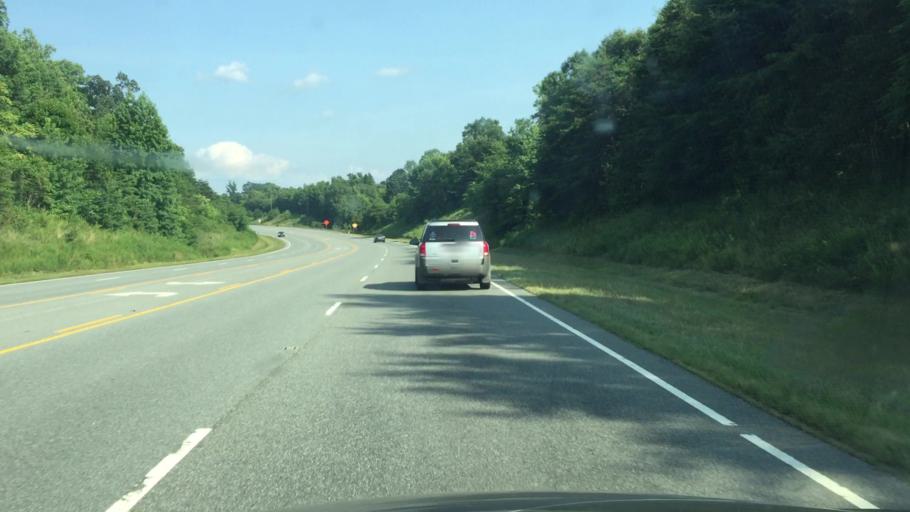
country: US
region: North Carolina
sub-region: Rockingham County
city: Reidsville
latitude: 36.3652
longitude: -79.6411
